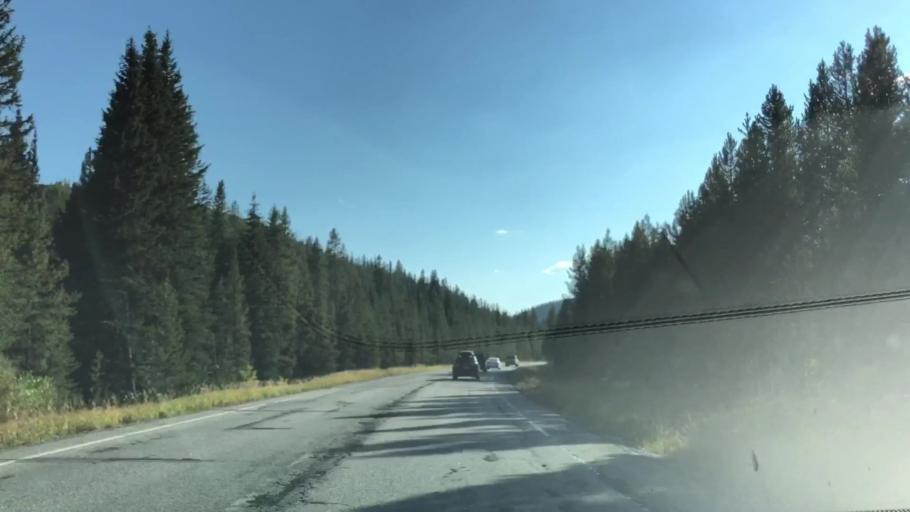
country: US
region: Montana
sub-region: Gallatin County
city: West Yellowstone
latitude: 44.8305
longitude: -111.0782
